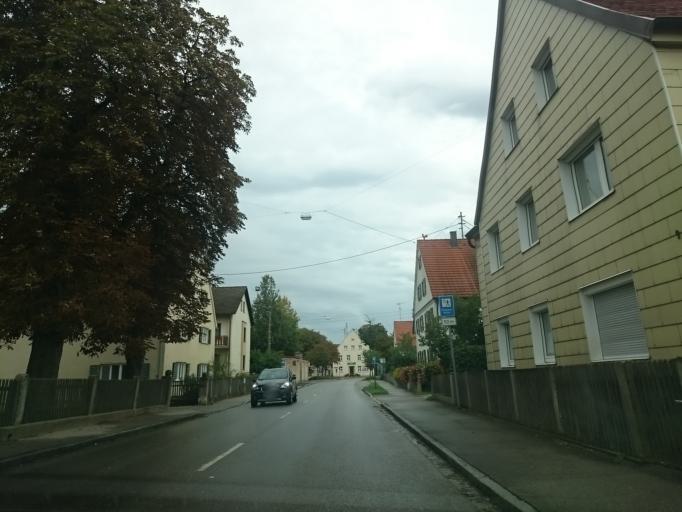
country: DE
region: Bavaria
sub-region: Swabia
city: Oberottmarshausen
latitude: 48.2371
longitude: 10.8565
